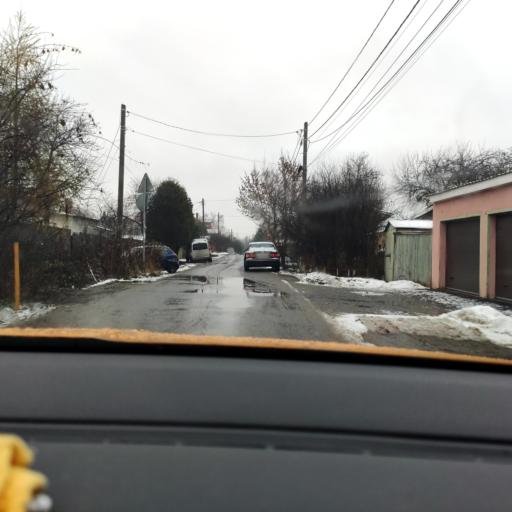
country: RU
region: Moskovskaya
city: Domodedovo
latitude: 55.4382
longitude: 37.7553
